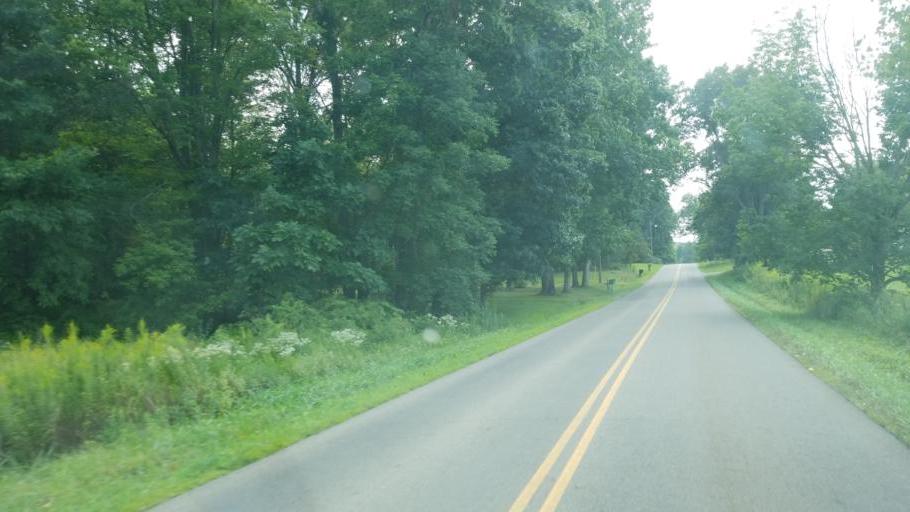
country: US
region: Ohio
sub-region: Knox County
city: Mount Vernon
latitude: 40.4471
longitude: -82.4870
